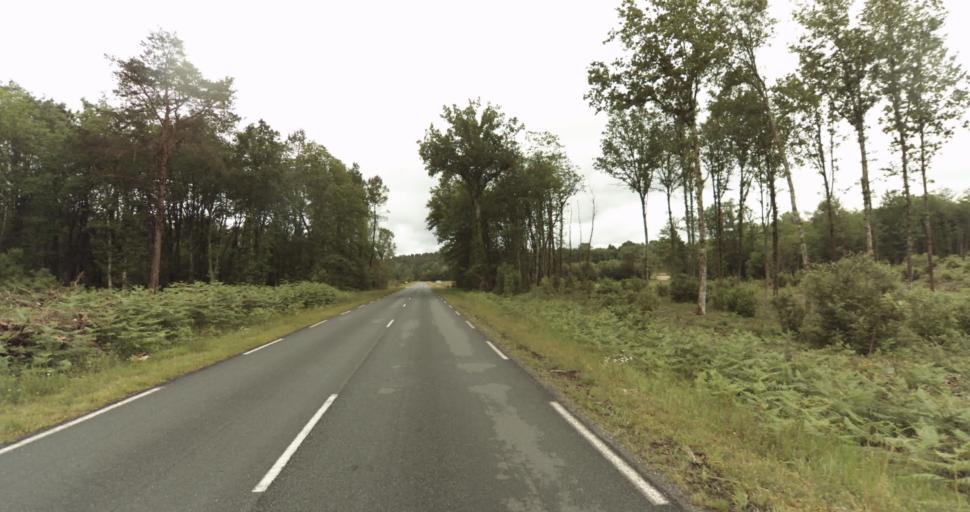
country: FR
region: Aquitaine
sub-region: Departement de la Dordogne
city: Belves
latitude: 44.6822
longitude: 0.9908
